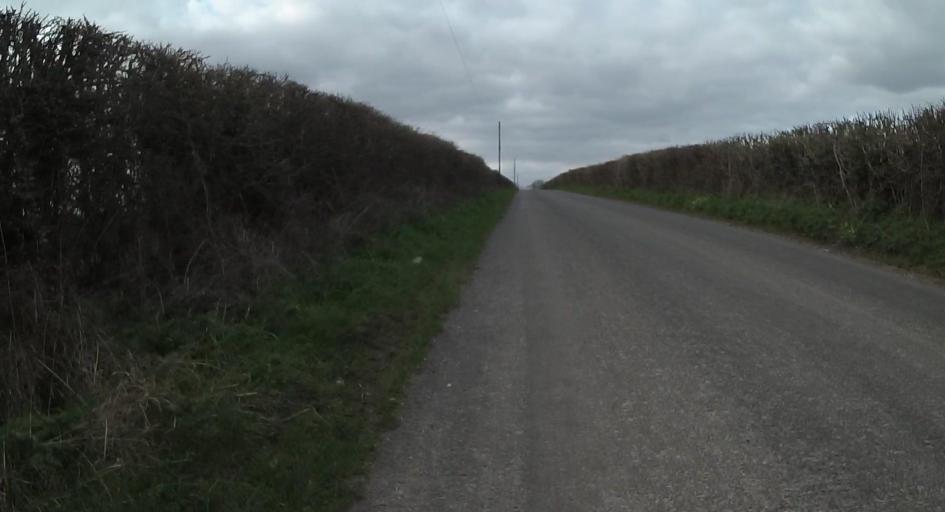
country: GB
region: England
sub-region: Hampshire
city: Abbotts Ann
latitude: 51.1440
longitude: -1.4850
